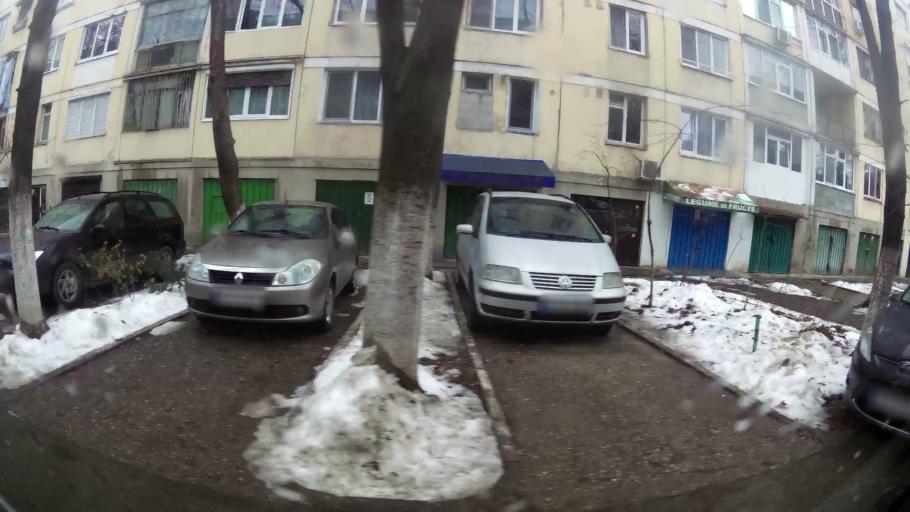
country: RO
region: Ilfov
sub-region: Comuna Chiajna
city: Rosu
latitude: 44.4165
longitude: 26.0164
